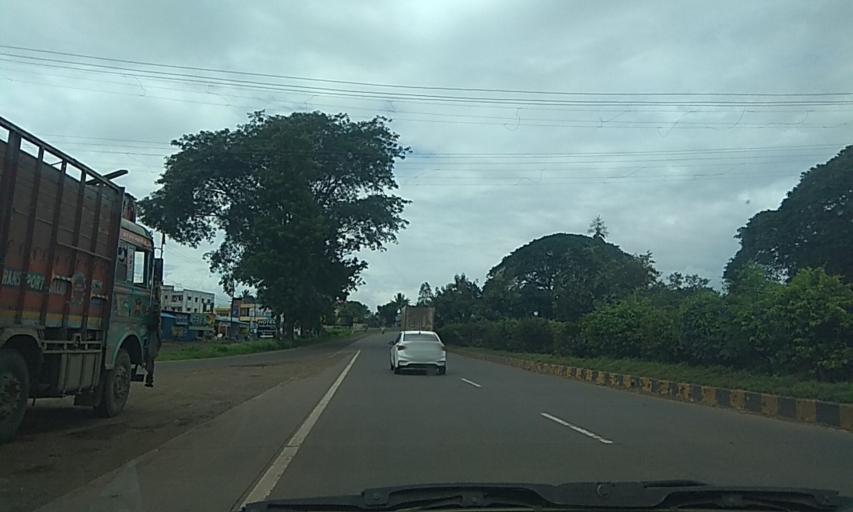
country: IN
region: Maharashtra
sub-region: Kolhapur
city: Kagal
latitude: 16.5811
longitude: 74.3112
